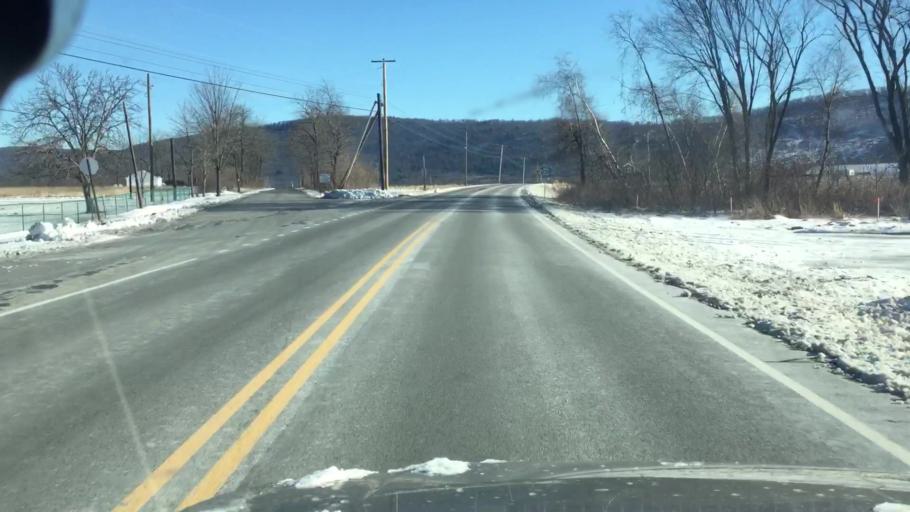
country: US
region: Pennsylvania
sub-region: Luzerne County
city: Nescopeck
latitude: 41.0436
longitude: -76.1436
